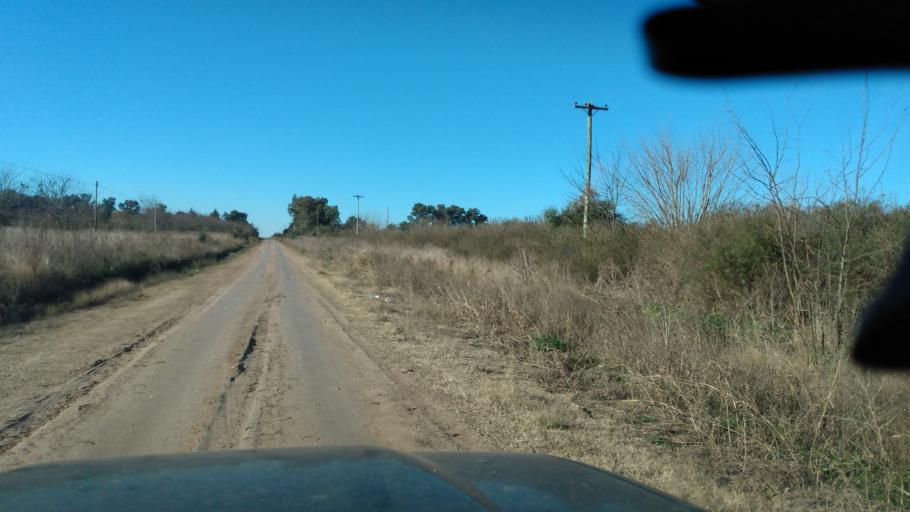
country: AR
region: Buenos Aires
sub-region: Partido de Lujan
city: Lujan
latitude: -34.5627
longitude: -59.1651
